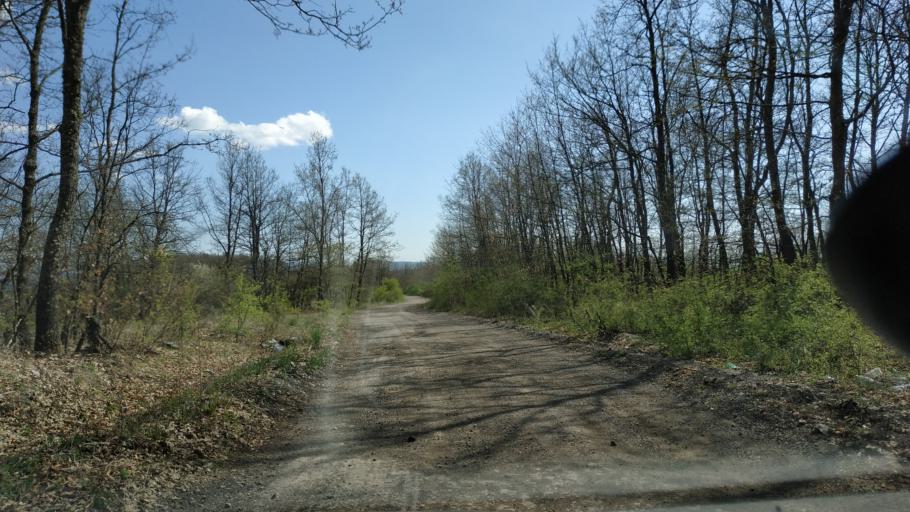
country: RS
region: Central Serbia
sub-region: Zajecarski Okrug
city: Soko Banja
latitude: 43.5349
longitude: 21.9062
